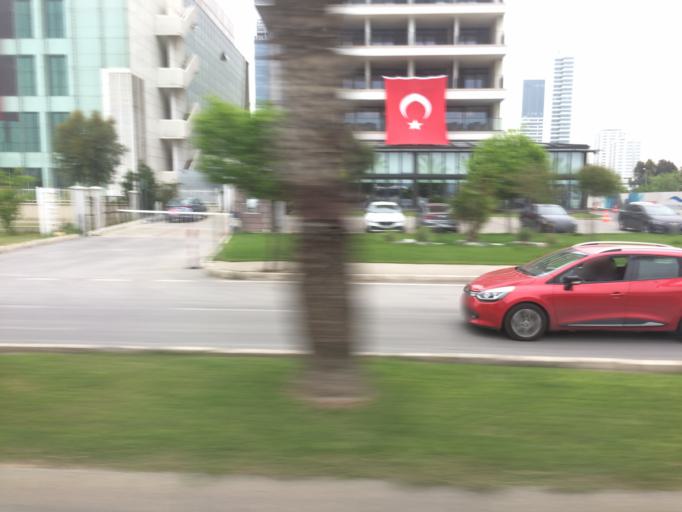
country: TR
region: Izmir
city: Izmir
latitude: 38.4500
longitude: 27.1705
